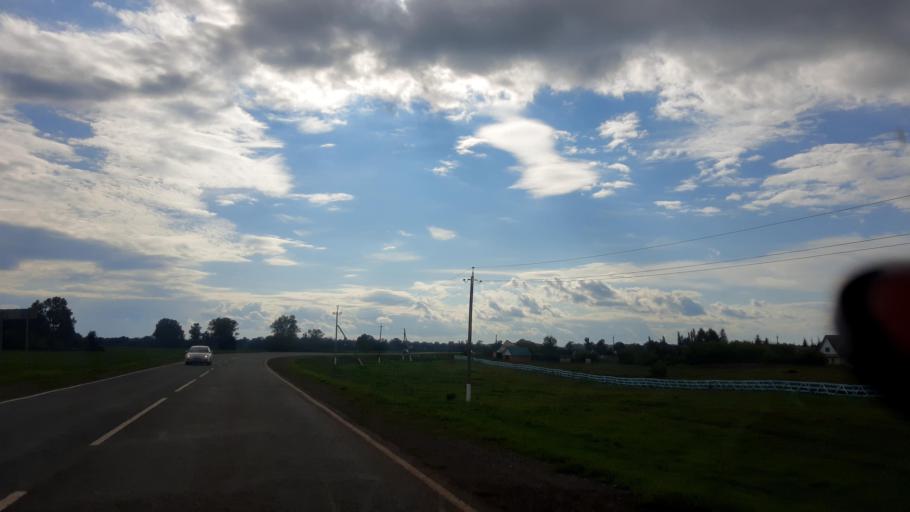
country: RU
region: Bashkortostan
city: Tolbazy
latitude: 53.9036
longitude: 56.3166
